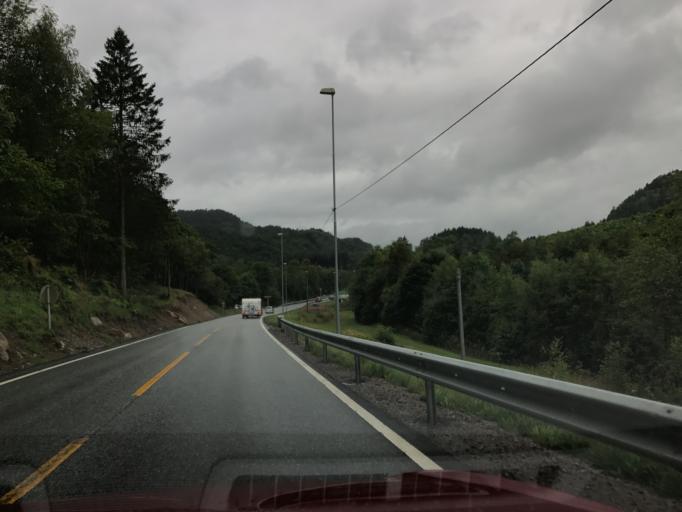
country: NO
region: Vest-Agder
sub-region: Lyngdal
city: Lyngdal
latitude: 58.1497
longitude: 7.1592
